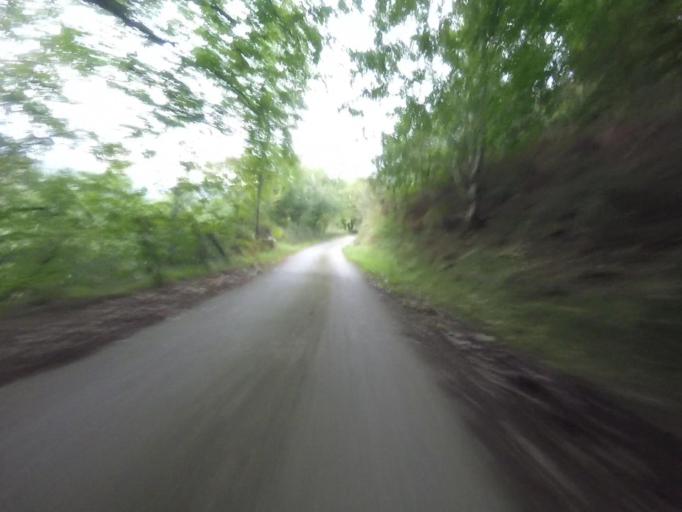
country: ES
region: Basque Country
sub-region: Provincia de Guipuzcoa
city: Errenteria
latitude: 43.2717
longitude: -1.8332
